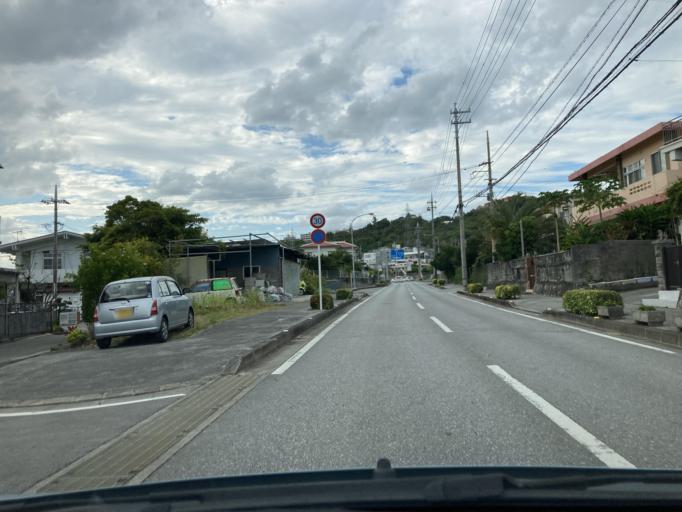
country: JP
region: Okinawa
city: Gushikawa
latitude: 26.3481
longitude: 127.8645
